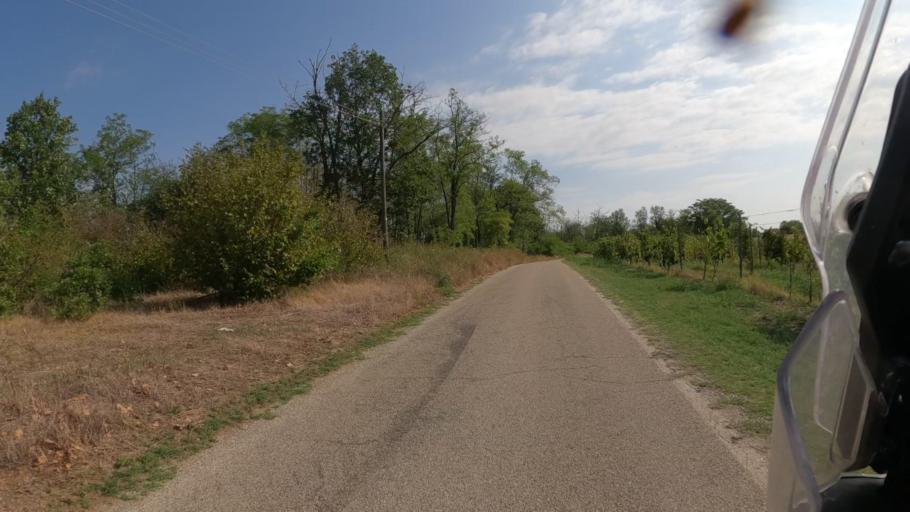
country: IT
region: Piedmont
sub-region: Provincia di Asti
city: Viarigi
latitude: 44.9582
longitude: 8.3747
